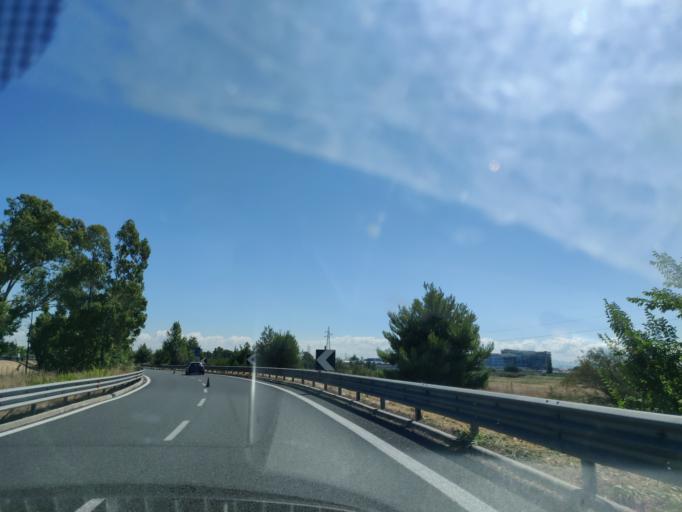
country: IT
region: Latium
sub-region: Citta metropolitana di Roma Capitale
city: Npp 23 (Parco Leonardo)
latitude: 41.8091
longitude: 12.3123
